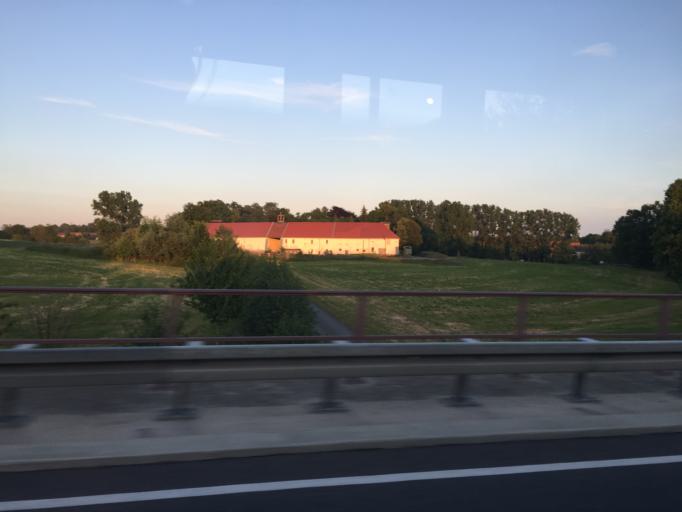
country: DE
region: Saxony
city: Sohland am Rotstein
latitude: 51.1383
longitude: 14.7700
